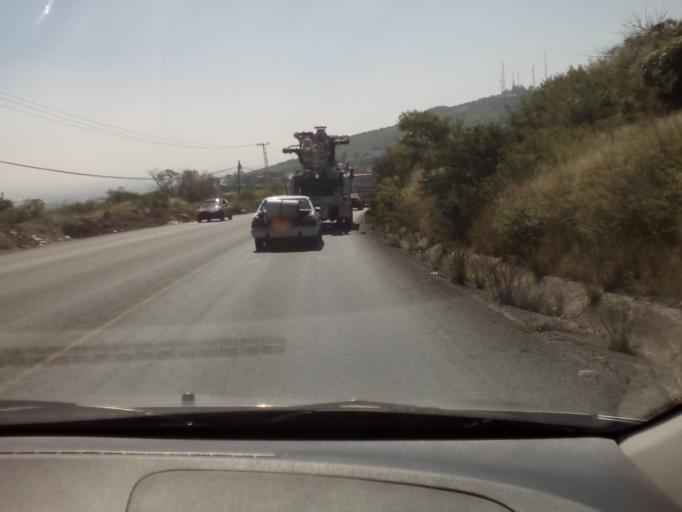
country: MX
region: Guanajuato
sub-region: Leon
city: La Ermita
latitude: 21.1762
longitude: -101.7236
